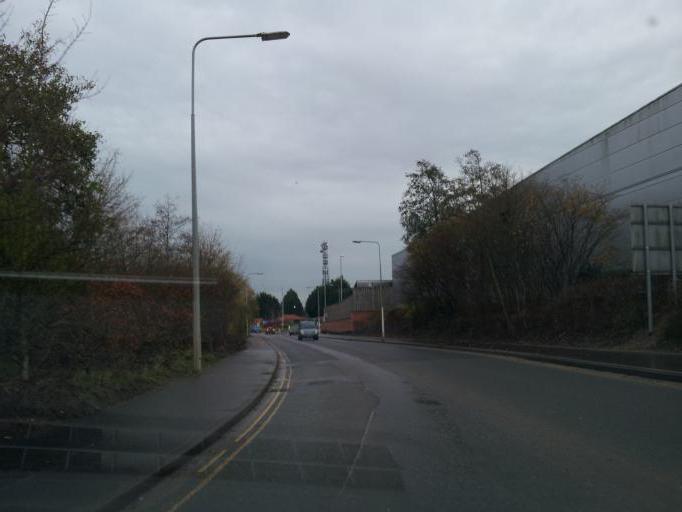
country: GB
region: England
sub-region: Norfolk
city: Costessey
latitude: 52.6537
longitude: 1.1831
